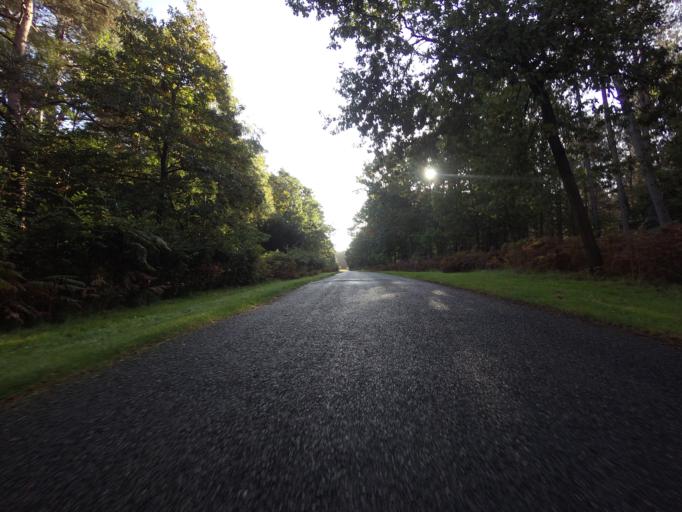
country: GB
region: England
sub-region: Norfolk
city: Dersingham
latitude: 52.8157
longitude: 0.5039
